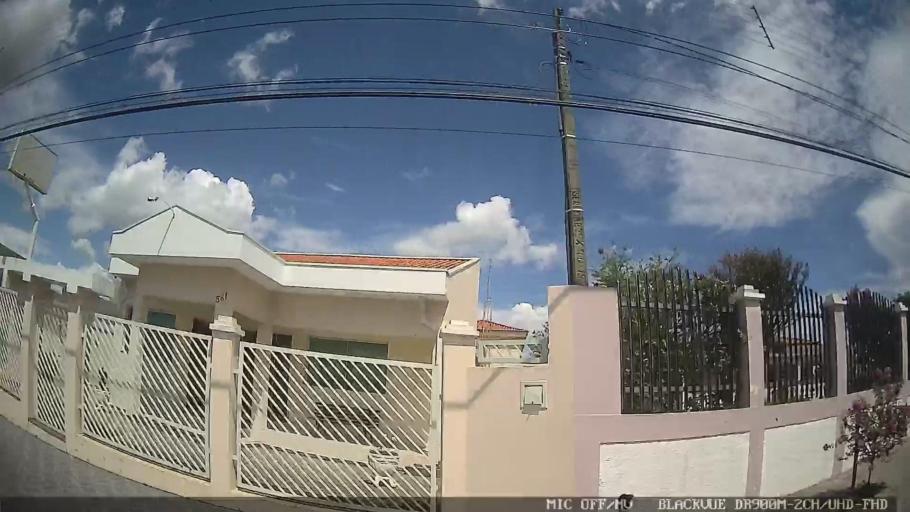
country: BR
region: Sao Paulo
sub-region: Conchas
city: Conchas
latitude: -23.0338
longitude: -48.0160
